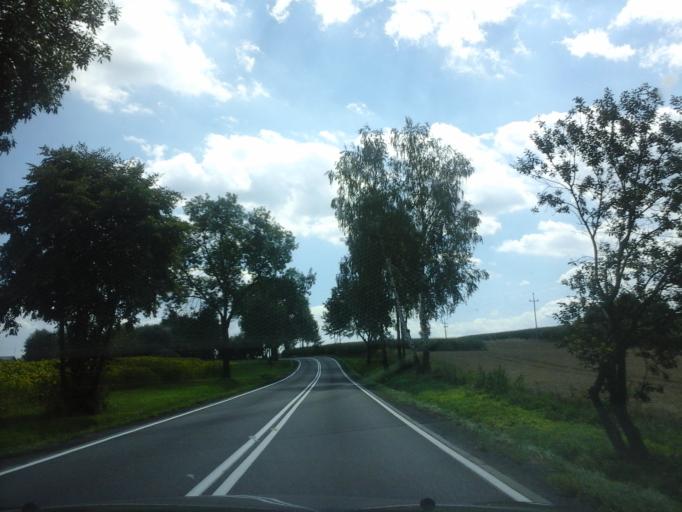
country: PL
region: Lesser Poland Voivodeship
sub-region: Powiat wadowicki
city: Spytkowice
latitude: 49.9895
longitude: 19.5226
